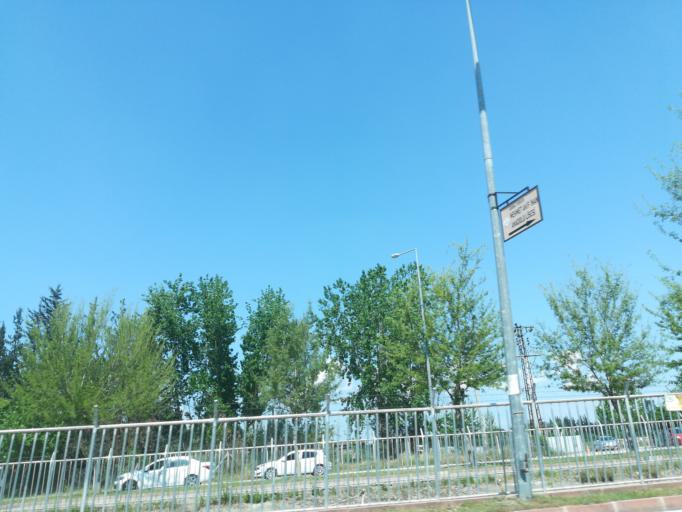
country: TR
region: Adana
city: Adana
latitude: 37.0261
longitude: 35.3614
